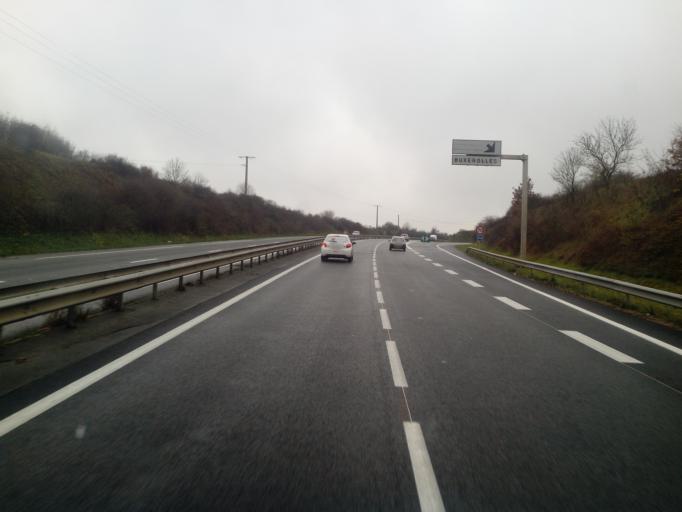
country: FR
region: Poitou-Charentes
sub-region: Departement de la Vienne
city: Chasseneuil-du-Poitou
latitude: 46.6149
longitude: 0.3735
